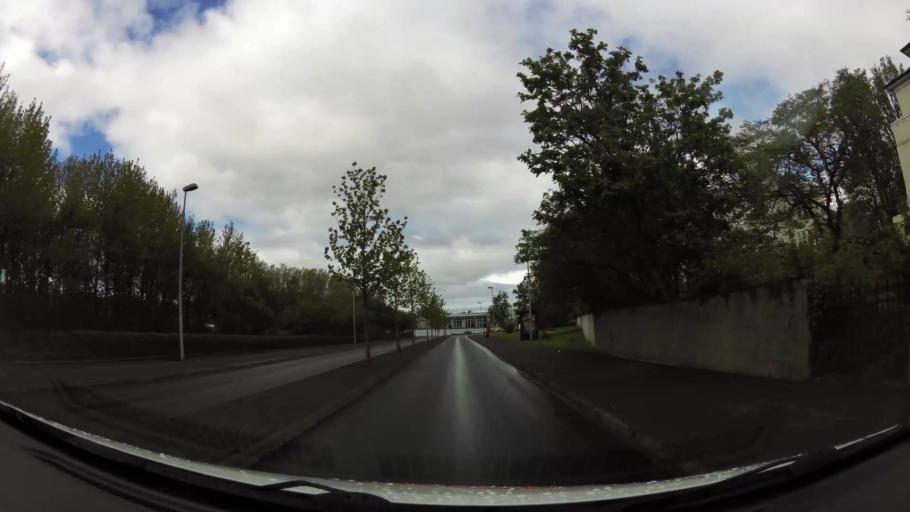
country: IS
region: Capital Region
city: Kopavogur
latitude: 64.1420
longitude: -21.9395
